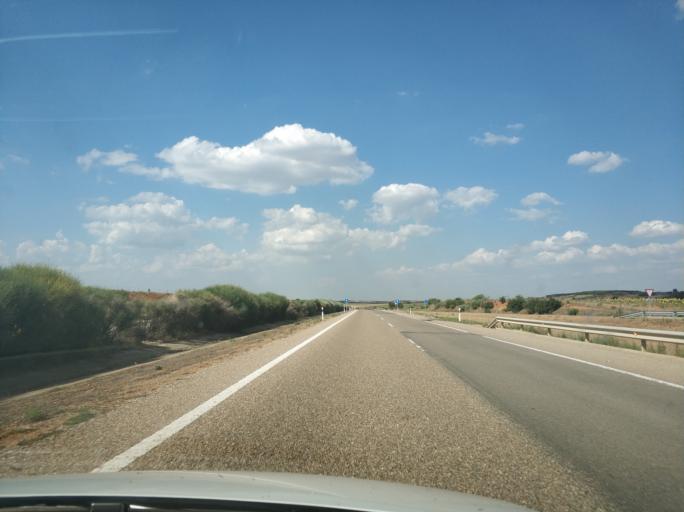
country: ES
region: Castille and Leon
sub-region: Provincia de Zamora
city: Matilla de Arzon
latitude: 42.1274
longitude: -5.6486
